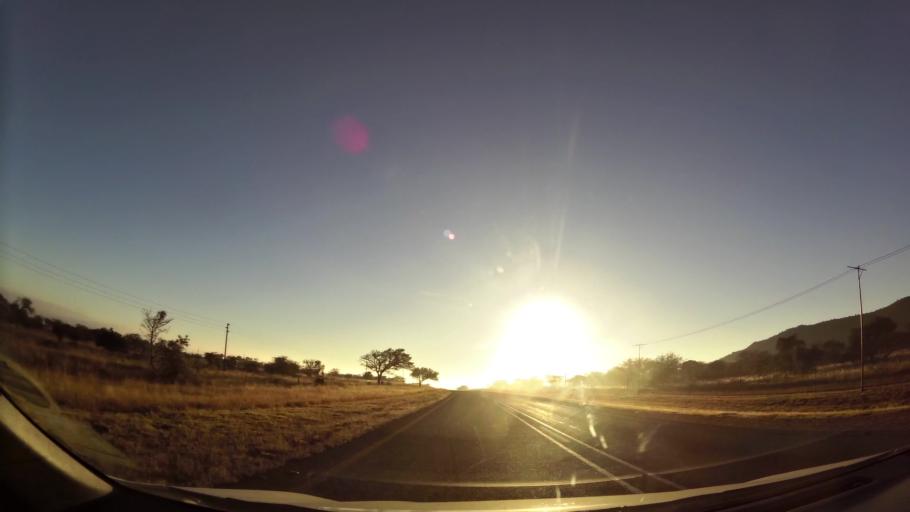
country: ZA
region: Limpopo
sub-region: Capricorn District Municipality
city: Polokwane
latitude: -24.0066
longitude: 29.3324
